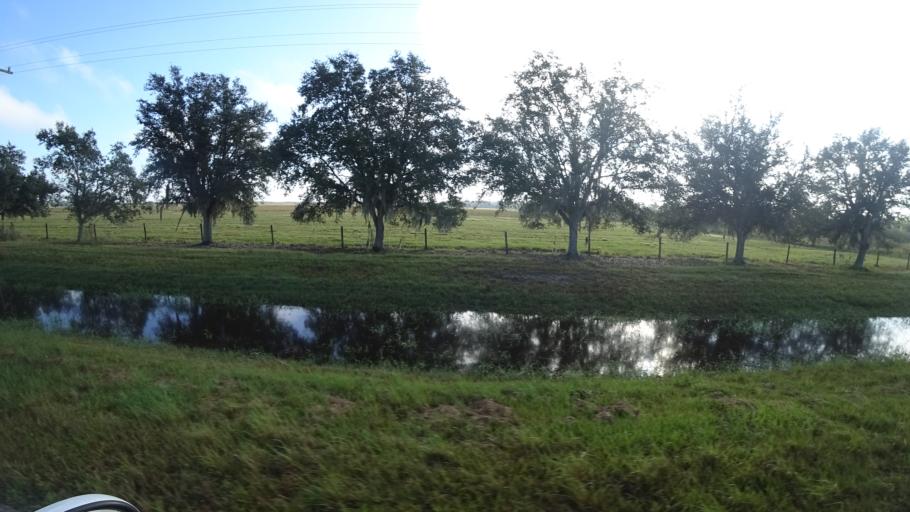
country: US
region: Florida
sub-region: Sarasota County
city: The Meadows
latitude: 27.4170
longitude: -82.3037
